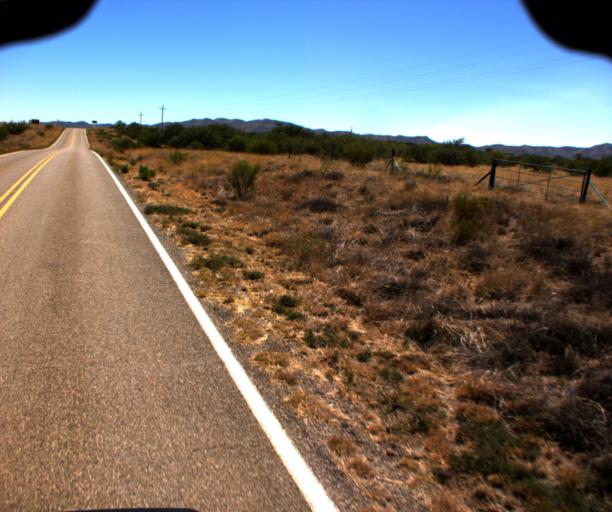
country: US
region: Arizona
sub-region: Pima County
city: Sells
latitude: 31.5916
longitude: -111.5301
